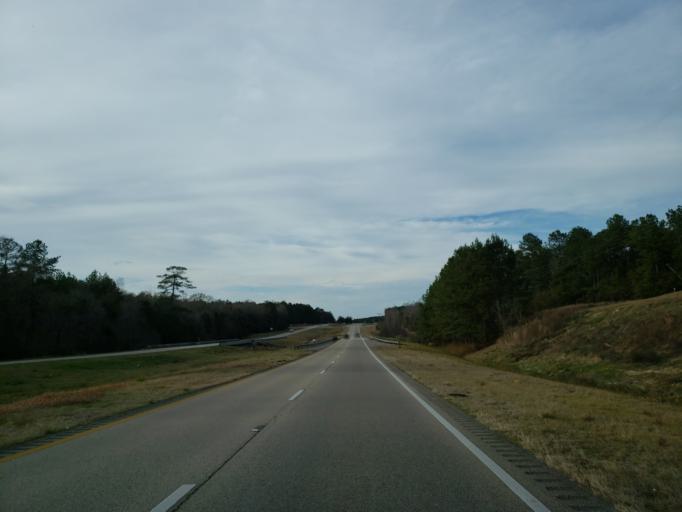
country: US
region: Mississippi
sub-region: Wayne County
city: Waynesboro
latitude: 31.6232
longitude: -88.5837
